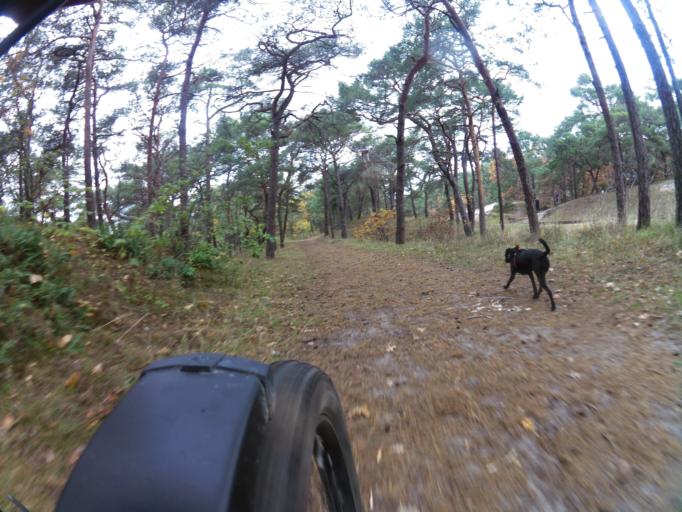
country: PL
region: Pomeranian Voivodeship
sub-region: Powiat pucki
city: Jastarnia
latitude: 54.6968
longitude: 18.6891
